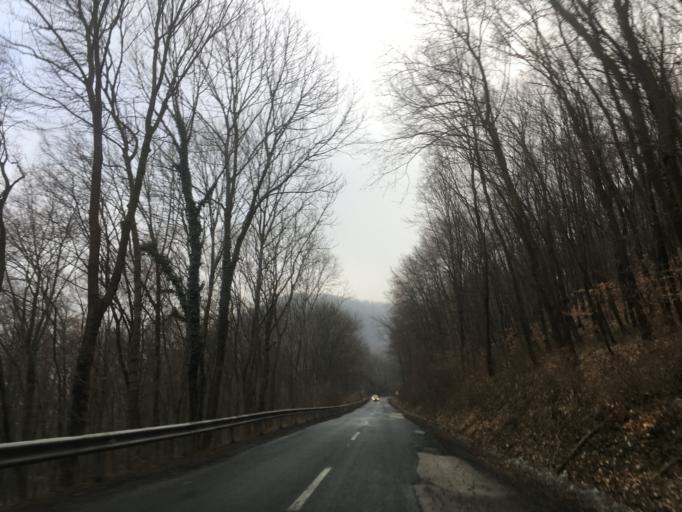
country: HU
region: Komarom-Esztergom
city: Kesztolc
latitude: 47.7229
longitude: 18.8420
